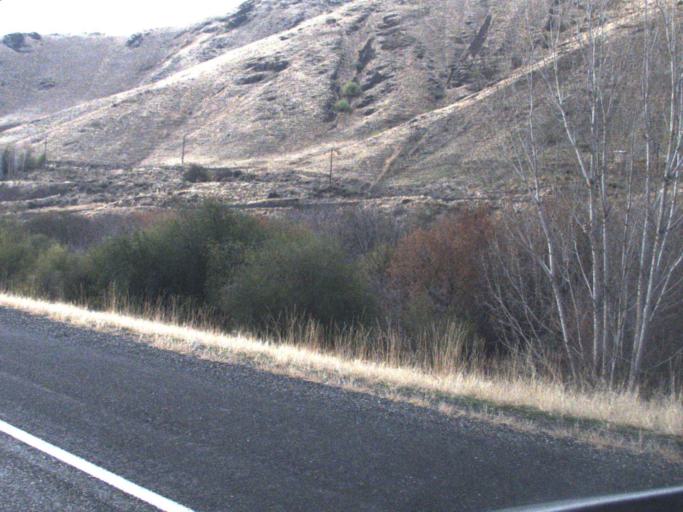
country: US
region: Washington
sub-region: Asotin County
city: Clarkston Heights-Vineland
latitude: 46.4137
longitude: -117.2117
